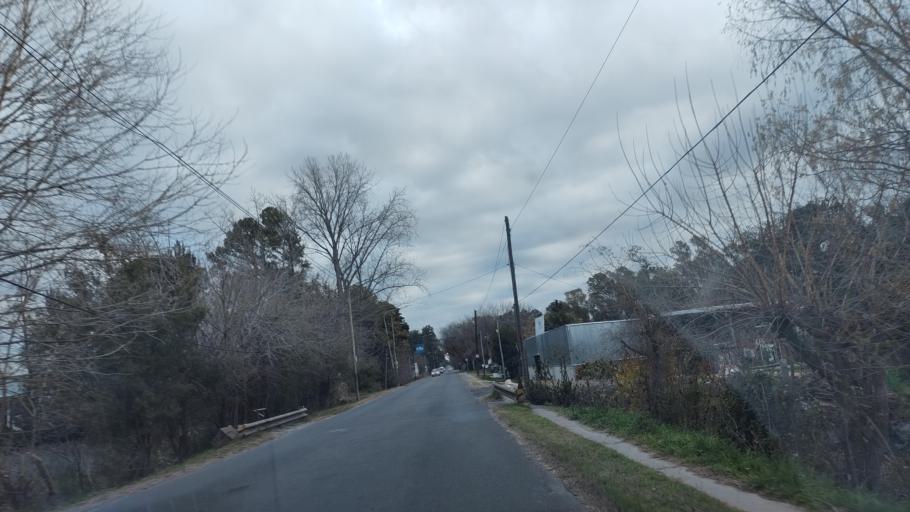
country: AR
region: Buenos Aires
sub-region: Partido de La Plata
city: La Plata
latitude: -34.8629
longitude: -58.0901
